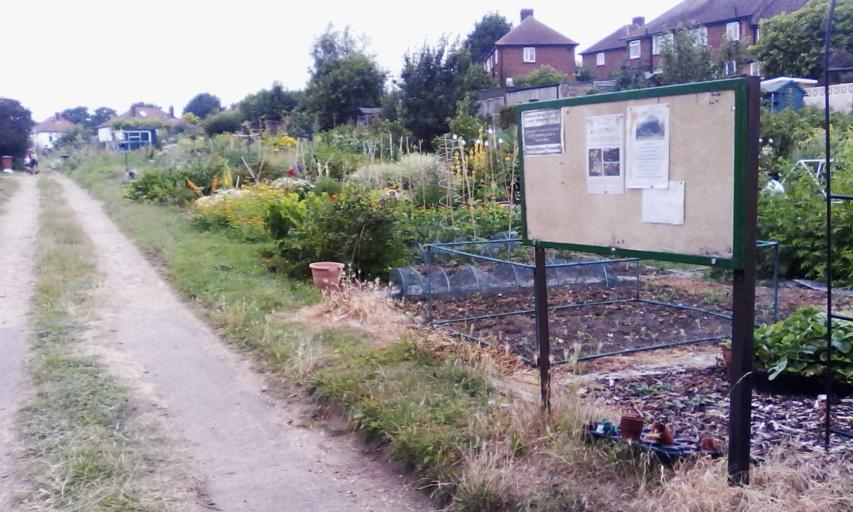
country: GB
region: England
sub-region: Hertfordshire
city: Ware
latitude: 51.8133
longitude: -0.0240
